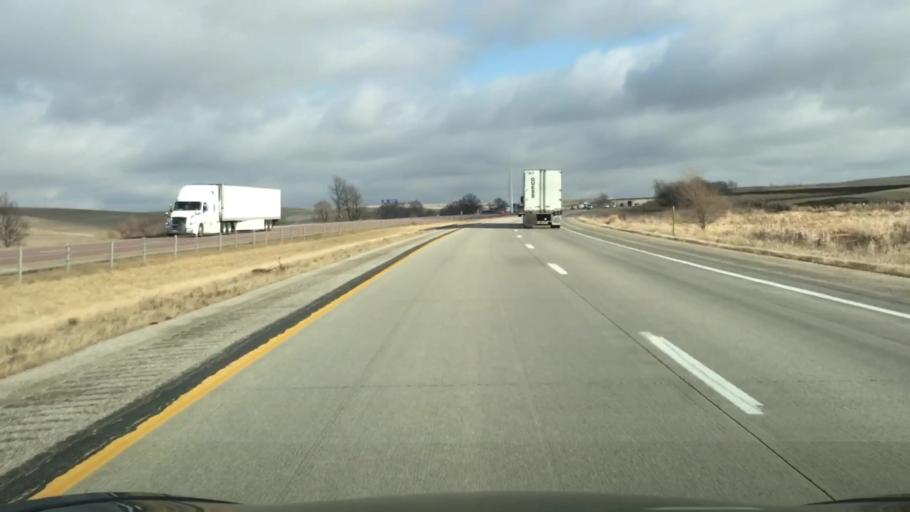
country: US
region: Iowa
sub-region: Guthrie County
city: Guthrie Center
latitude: 41.4963
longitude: -94.5803
